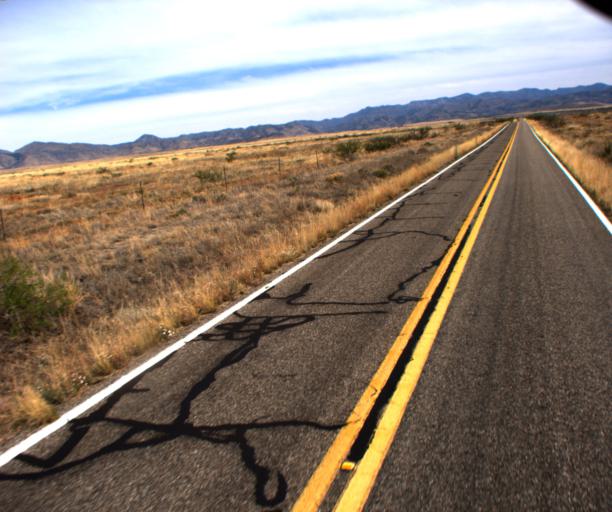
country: US
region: Arizona
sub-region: Cochise County
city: Willcox
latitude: 32.0553
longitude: -109.4963
